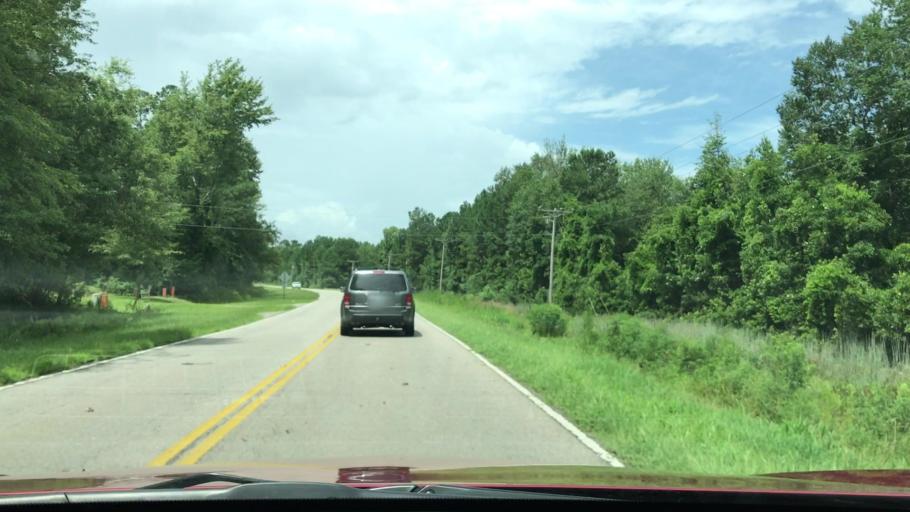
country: US
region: South Carolina
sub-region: Horry County
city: Red Hill
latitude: 33.9039
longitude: -78.9109
